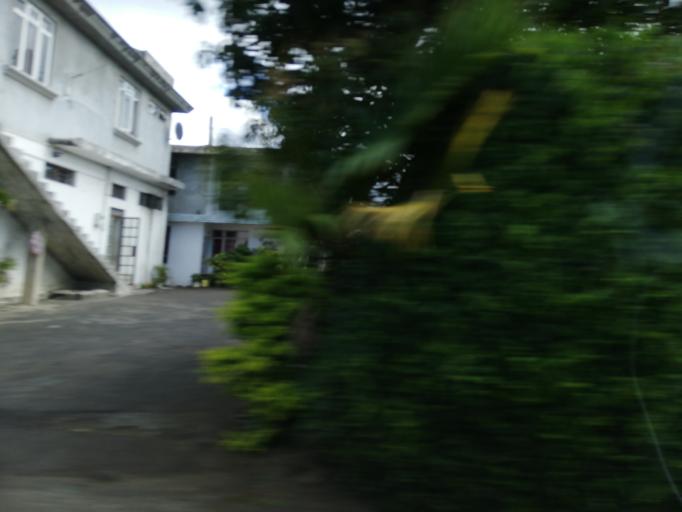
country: MU
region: Flacq
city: Camp de Masque
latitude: -20.2341
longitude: 57.6800
